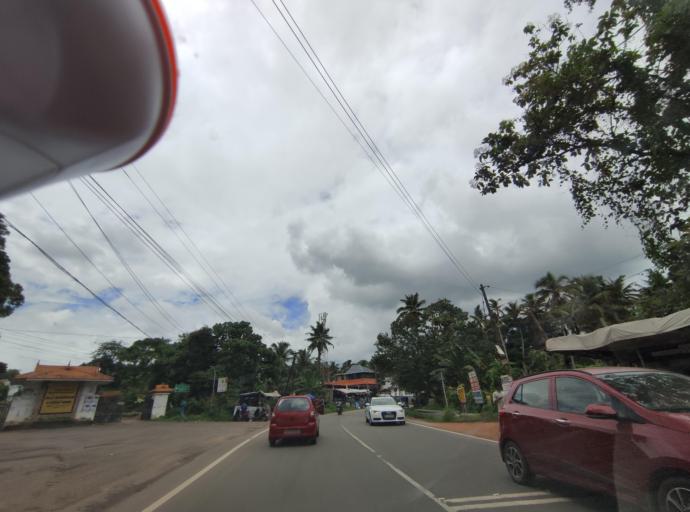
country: IN
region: Kerala
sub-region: Thiruvananthapuram
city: Nedumangad
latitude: 8.5668
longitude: 76.9442
